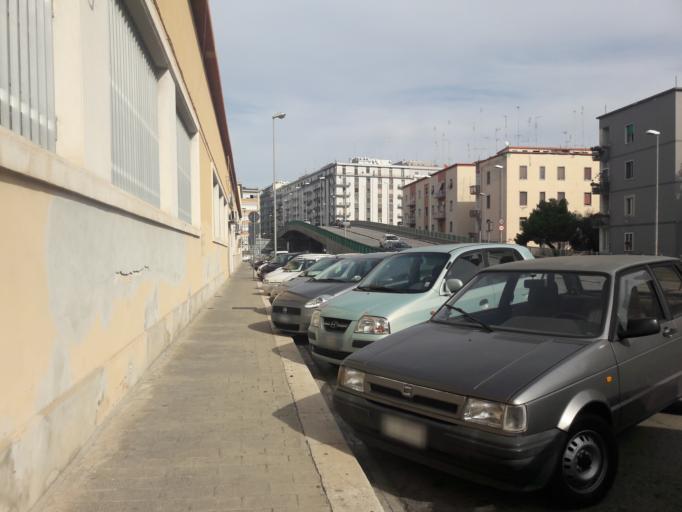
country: IT
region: Apulia
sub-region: Provincia di Bari
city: Bari
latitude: 41.1158
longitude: 16.8878
